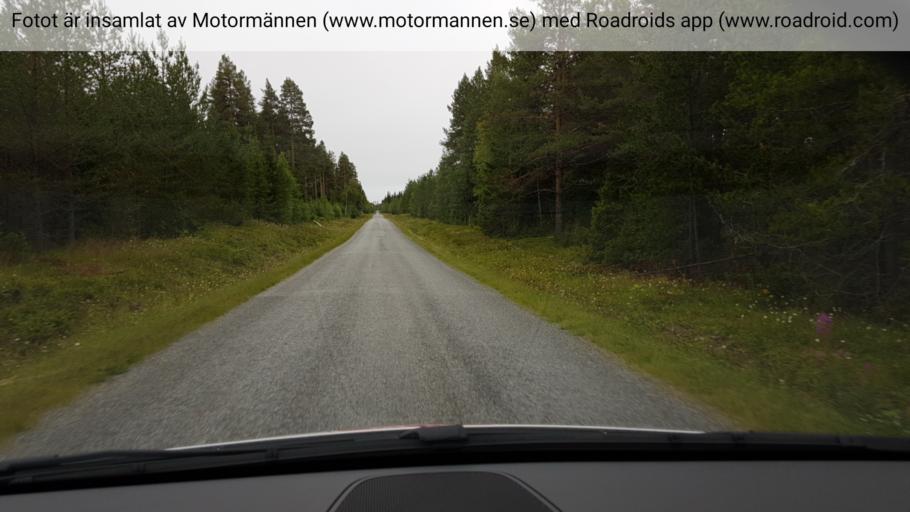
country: SE
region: Jaemtland
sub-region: OEstersunds Kommun
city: Lit
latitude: 63.8730
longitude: 14.9187
